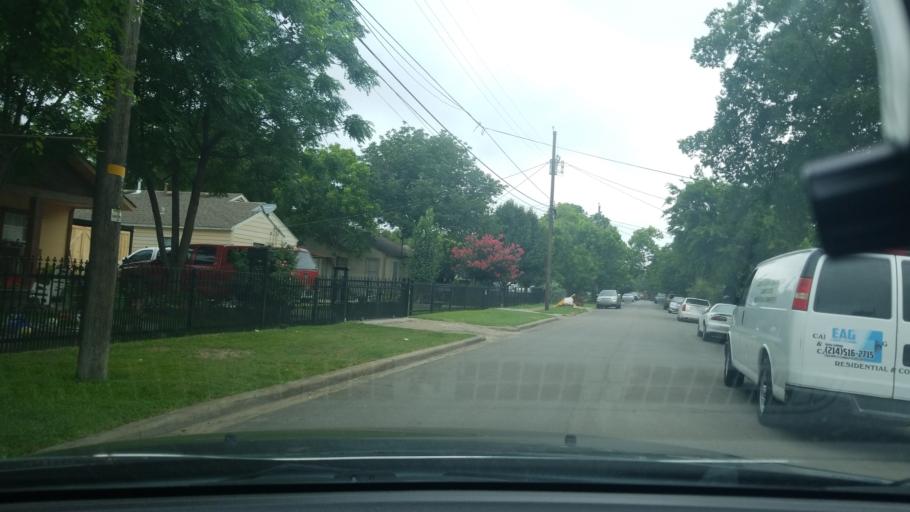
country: US
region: Texas
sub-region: Dallas County
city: Balch Springs
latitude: 32.7732
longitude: -96.6908
